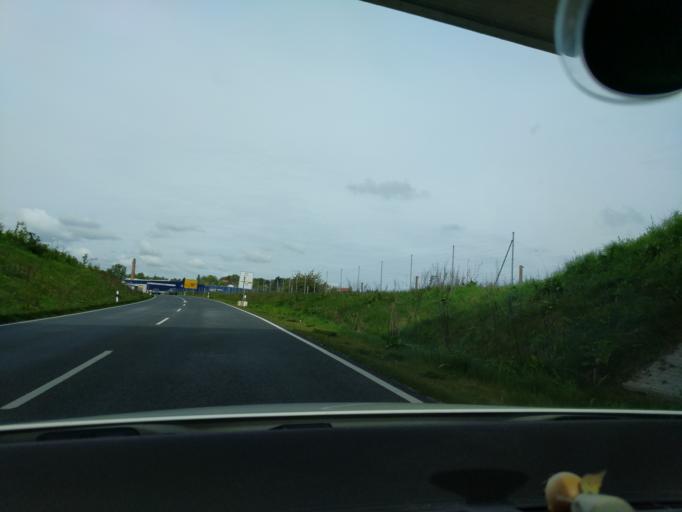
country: DE
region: Saxony
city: Bannewitz
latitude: 50.9898
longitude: 13.7197
